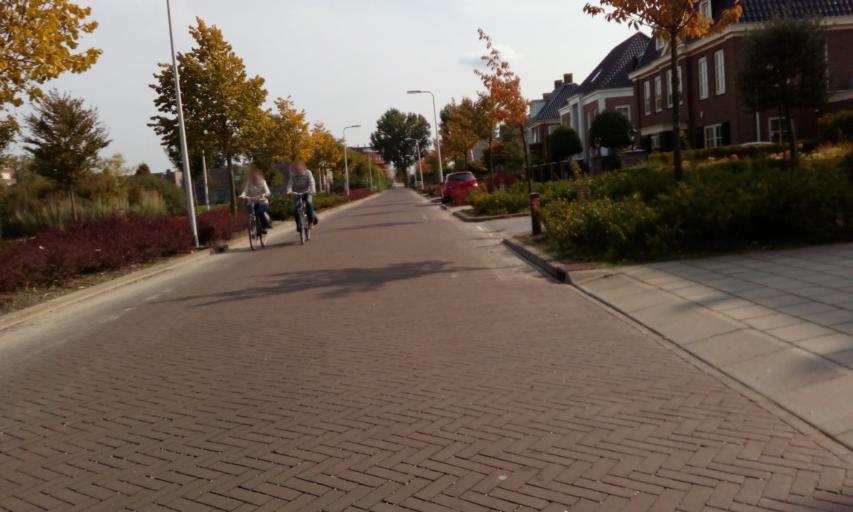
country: NL
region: South Holland
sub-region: Gemeente Westland
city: Kwintsheul
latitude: 52.0244
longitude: 4.2851
